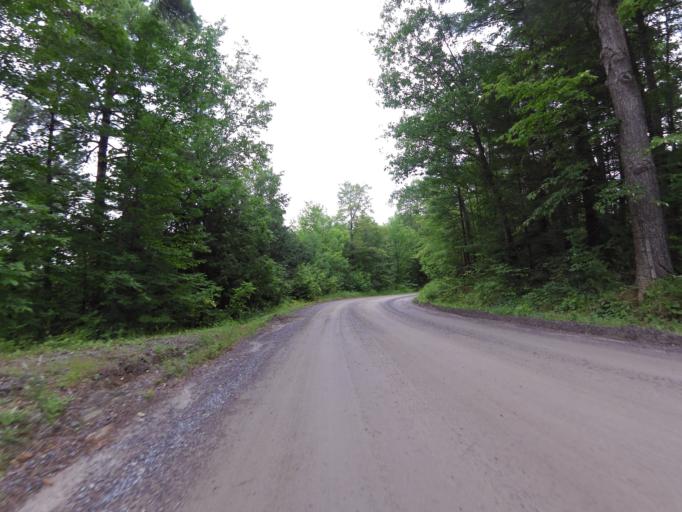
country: CA
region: Ontario
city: Kingston
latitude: 44.5588
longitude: -76.6018
